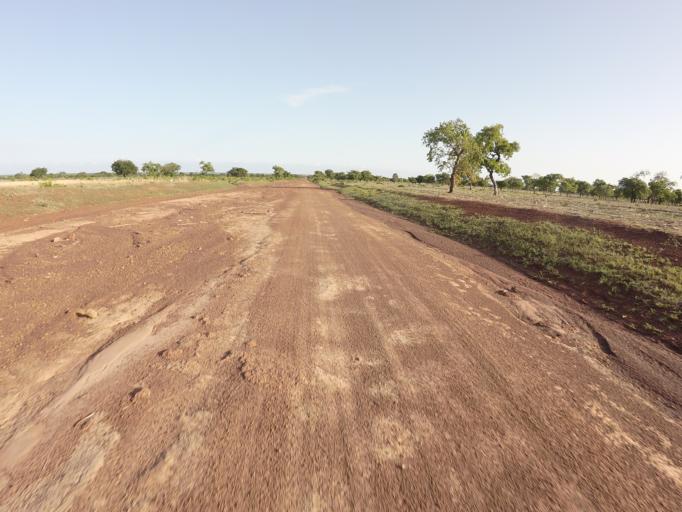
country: TG
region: Savanes
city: Sansanne-Mango
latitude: 10.3822
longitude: -0.0948
